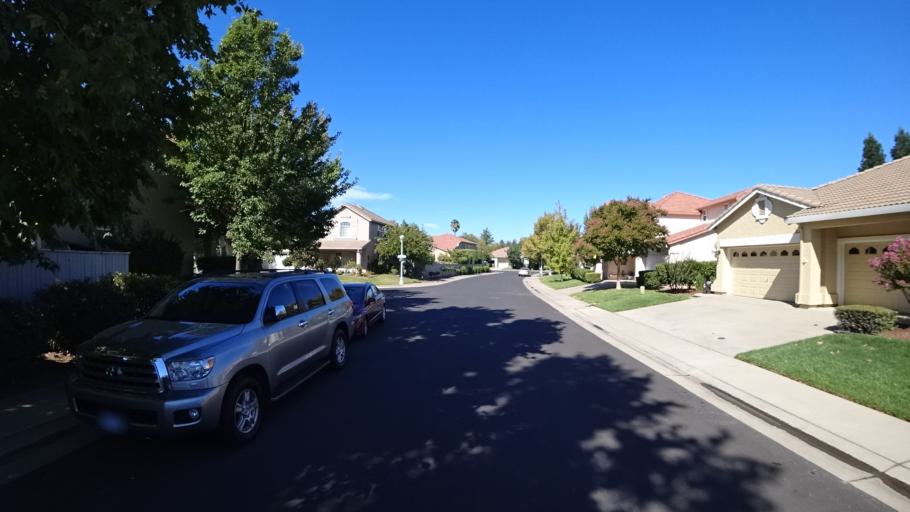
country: US
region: California
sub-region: Sacramento County
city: Laguna
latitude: 38.4188
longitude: -121.4744
